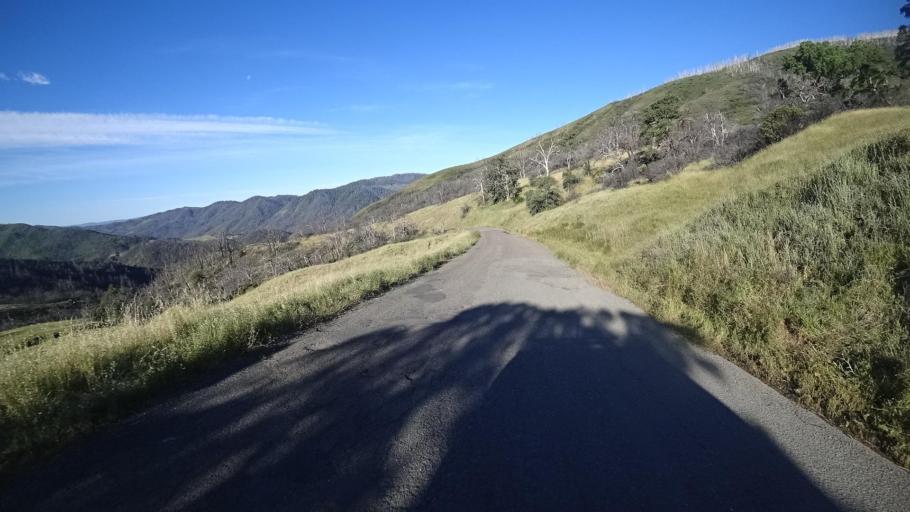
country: US
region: California
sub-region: Lake County
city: Upper Lake
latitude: 39.2706
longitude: -122.9246
